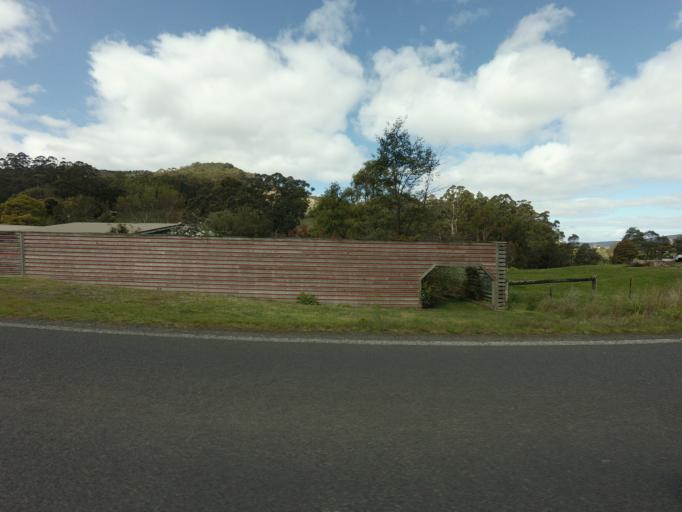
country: AU
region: Tasmania
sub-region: Huon Valley
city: Geeveston
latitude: -43.3008
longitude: 147.0076
